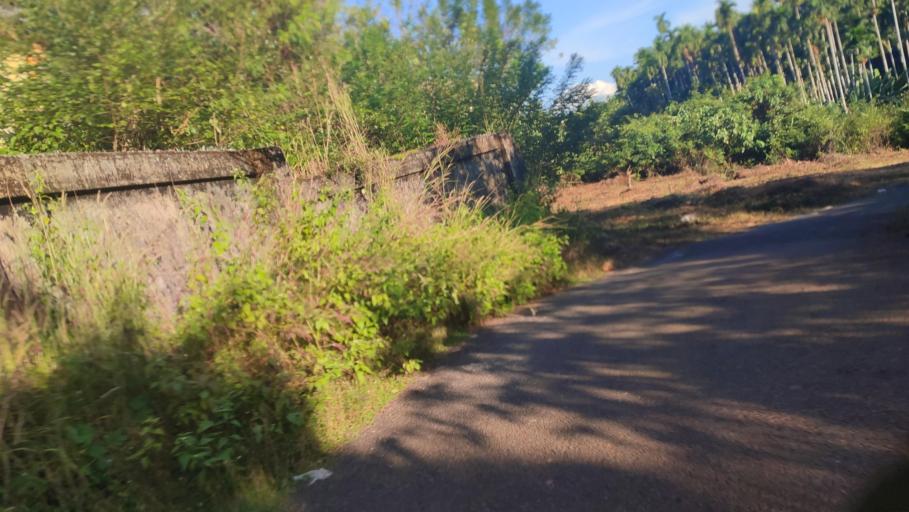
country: IN
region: Kerala
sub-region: Kasaragod District
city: Kasaragod
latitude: 12.5029
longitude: 75.0790
